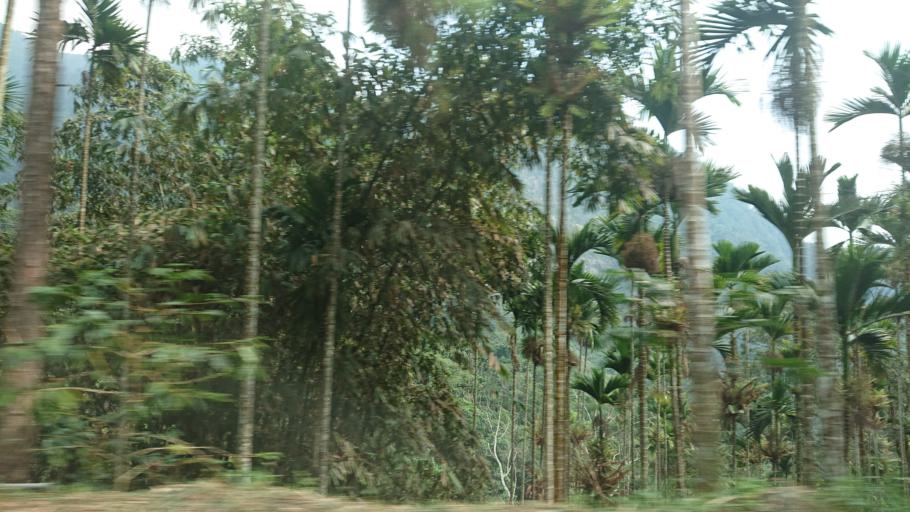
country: TW
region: Taiwan
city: Lugu
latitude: 23.5927
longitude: 120.6998
